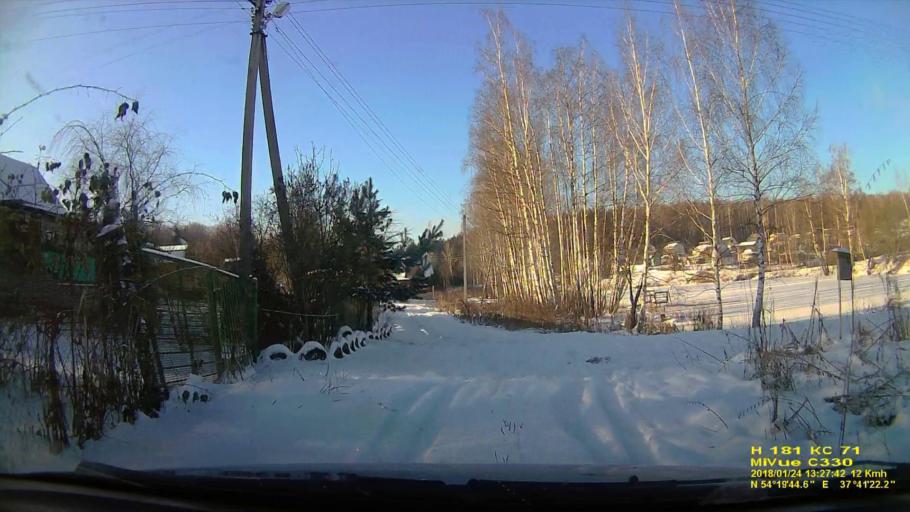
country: RU
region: Tula
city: Revyakino
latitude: 54.3294
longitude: 37.6897
